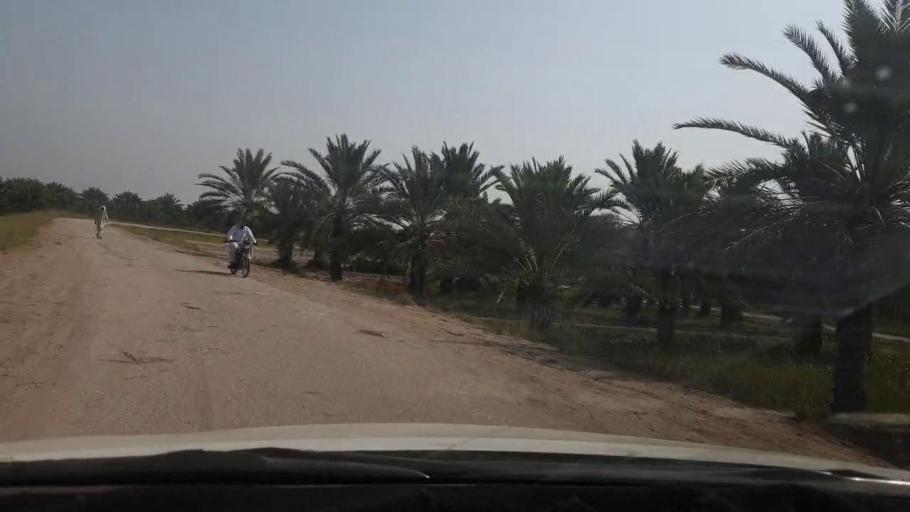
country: PK
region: Sindh
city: Rohri
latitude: 27.5886
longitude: 68.8739
